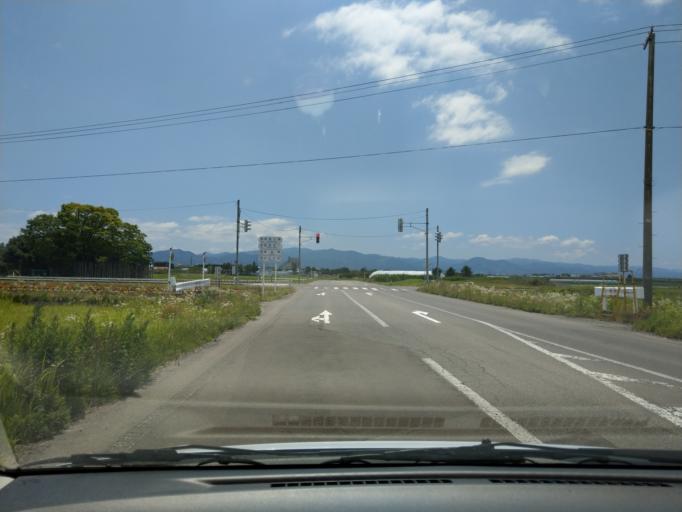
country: JP
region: Aomori
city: Kuroishi
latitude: 40.6231
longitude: 140.5631
